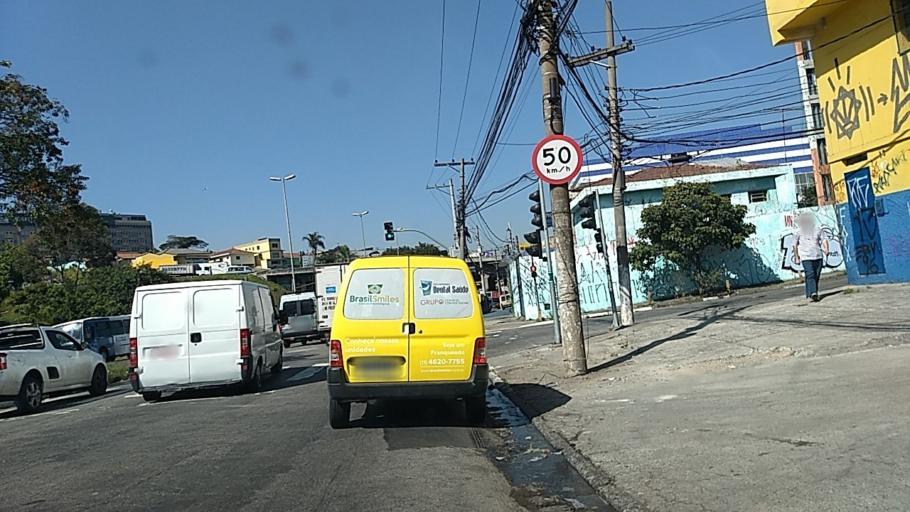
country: BR
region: Sao Paulo
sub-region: Guarulhos
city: Guarulhos
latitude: -23.5061
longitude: -46.5722
